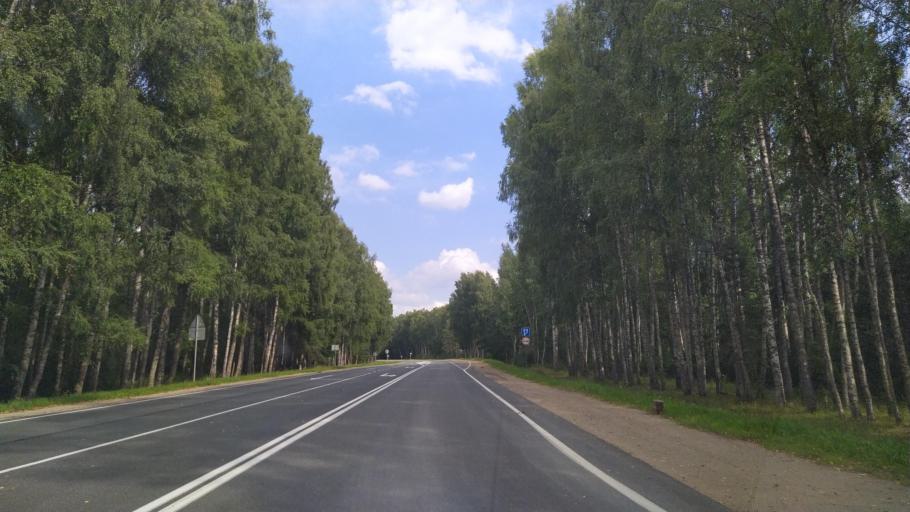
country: RU
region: Pskov
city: Dno
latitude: 57.9829
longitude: 29.7869
